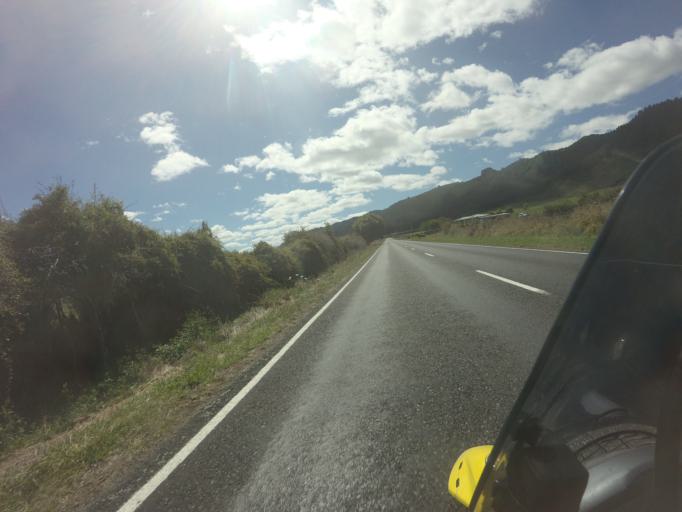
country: NZ
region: Bay of Plenty
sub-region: Kawerau District
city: Kawerau
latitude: -38.2143
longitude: 176.8440
